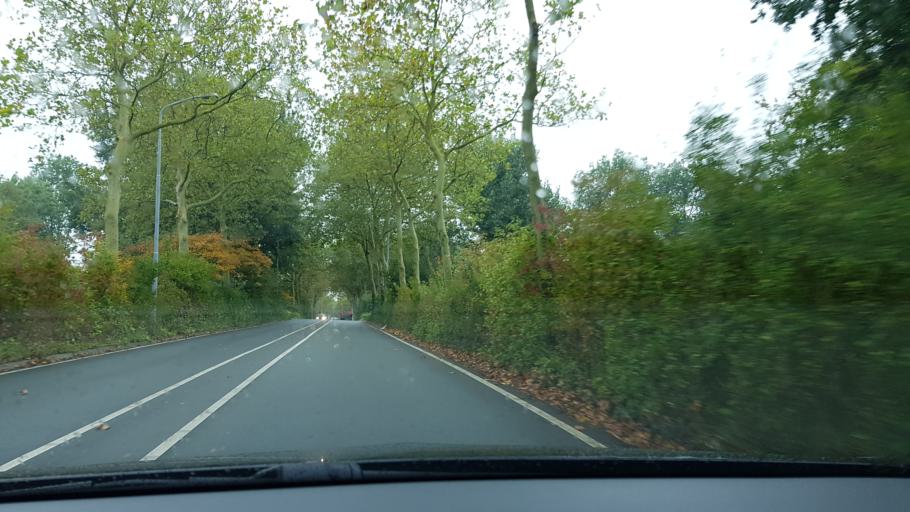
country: NL
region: North Holland
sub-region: Gemeente Haarlemmermeer
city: Hoofddorp
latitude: 52.3074
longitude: 4.6798
